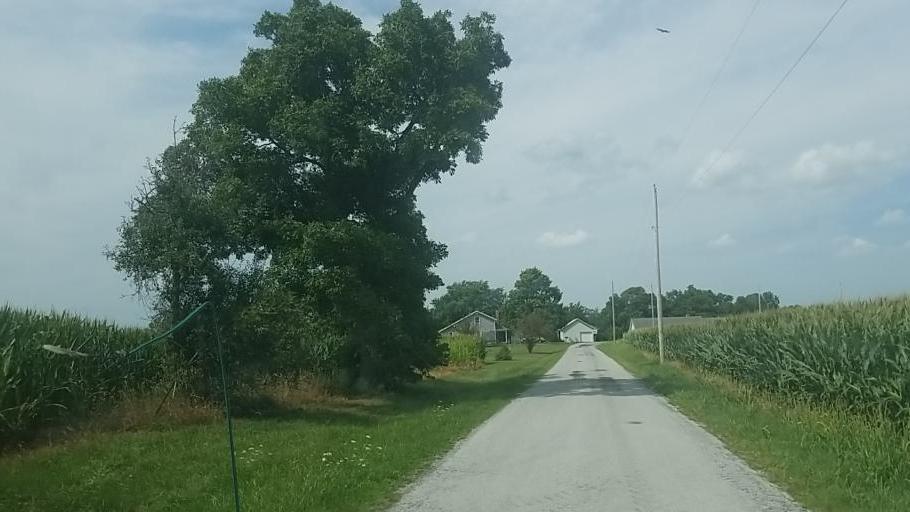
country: US
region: Ohio
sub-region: Hardin County
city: Forest
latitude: 40.7880
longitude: -83.5604
